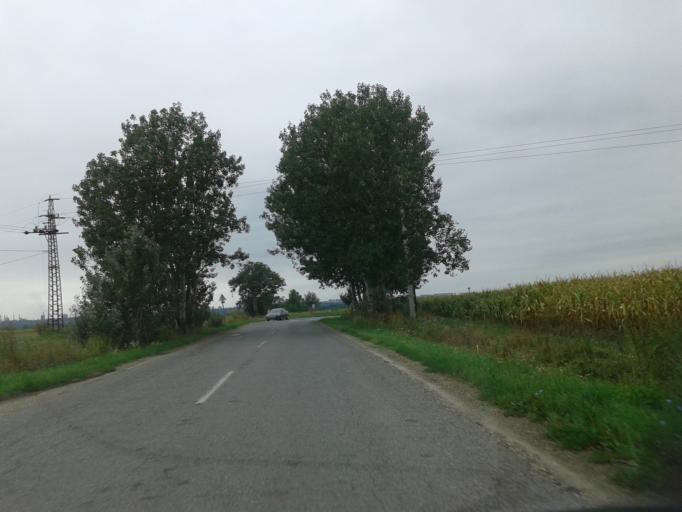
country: HU
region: Bacs-Kiskun
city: Szalkszentmarton
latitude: 46.9728
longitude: 19.0009
